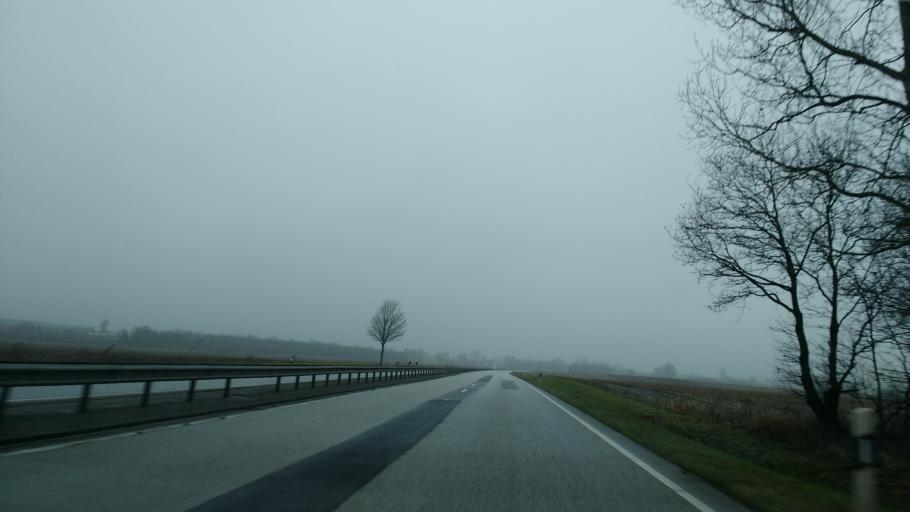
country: DE
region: Schleswig-Holstein
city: Jevenstedt
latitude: 54.2418
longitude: 9.6742
